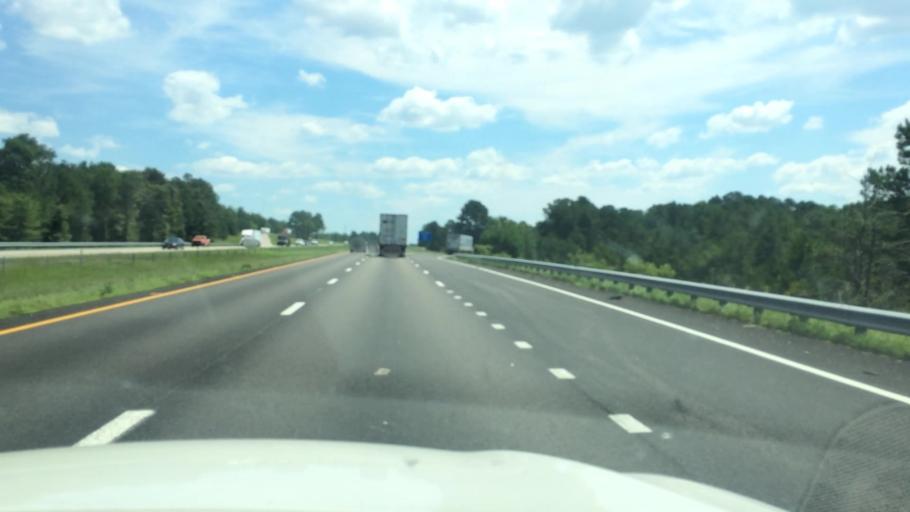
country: US
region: South Carolina
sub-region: Aiken County
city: Aiken
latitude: 33.6503
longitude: -81.7132
